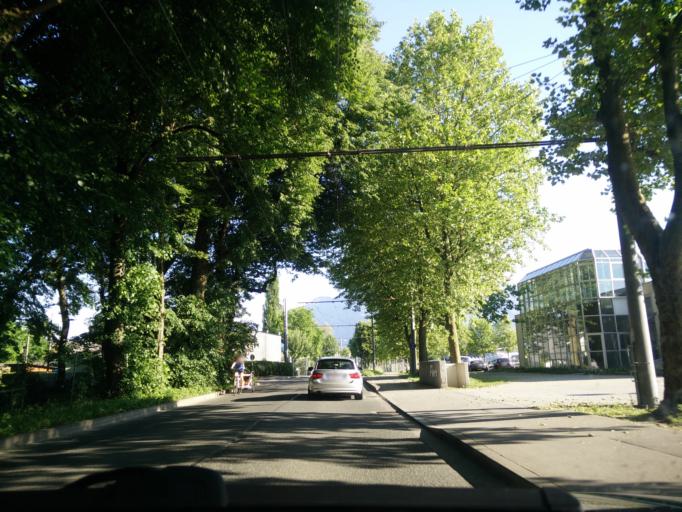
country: AT
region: Salzburg
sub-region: Salzburg Stadt
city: Salzburg
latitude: 47.7948
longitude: 13.0085
